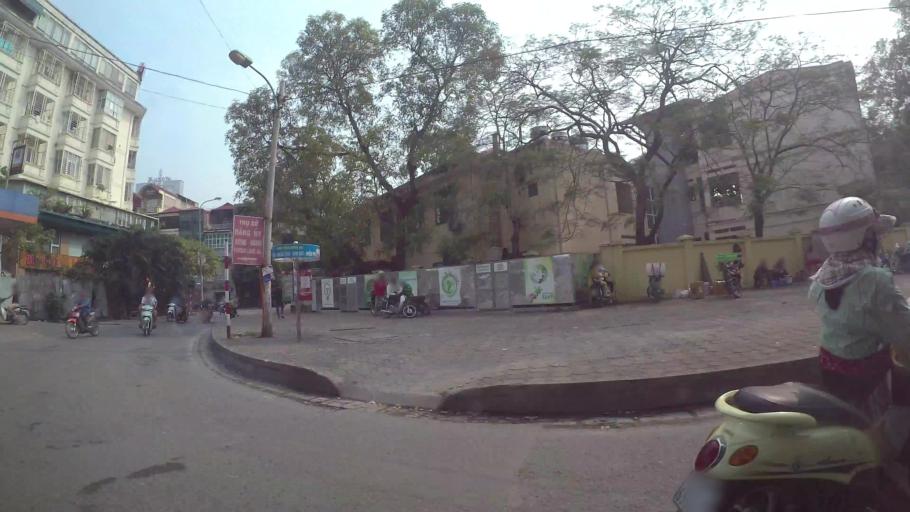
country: VN
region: Ha Noi
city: Cau Giay
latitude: 21.0151
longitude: 105.8093
